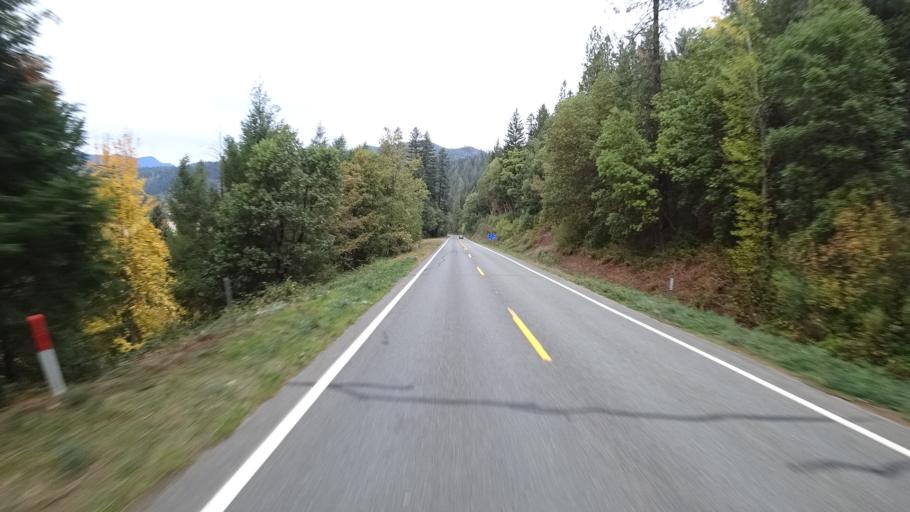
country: US
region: California
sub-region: Siskiyou County
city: Happy Camp
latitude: 41.8038
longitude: -123.3456
